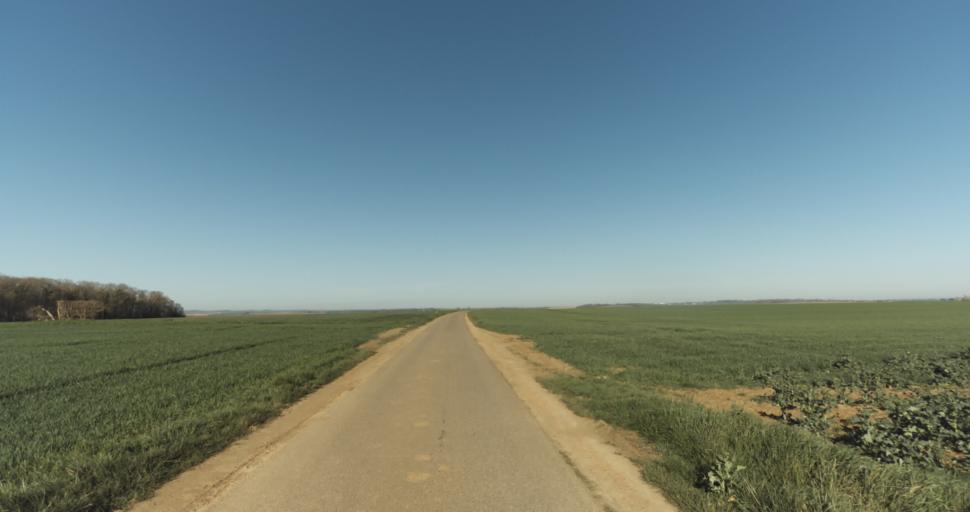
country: FR
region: Lower Normandy
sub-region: Departement du Calvados
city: Saint-Pierre-sur-Dives
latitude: 48.9914
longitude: -0.0359
